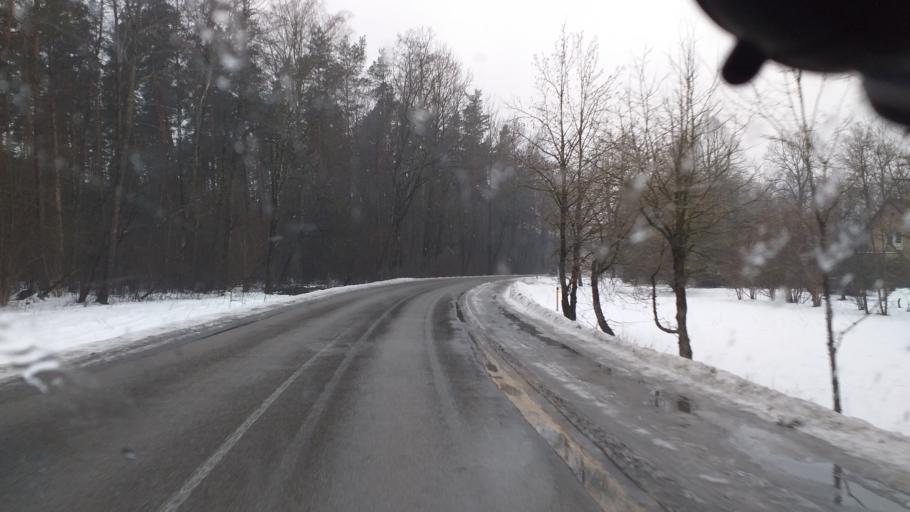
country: LV
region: Riga
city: Daugavgriva
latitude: 56.9831
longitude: 23.9981
